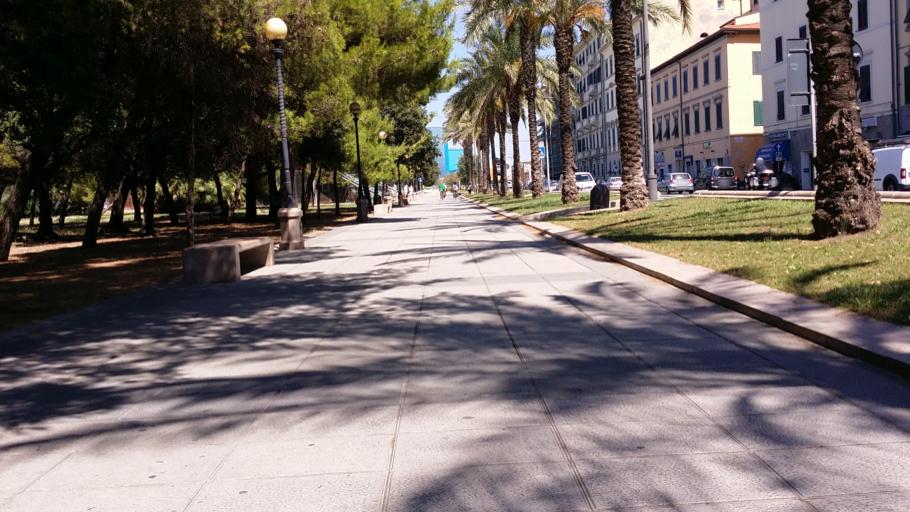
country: IT
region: Tuscany
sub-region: Provincia di Livorno
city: Livorno
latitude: 43.5385
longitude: 10.3019
